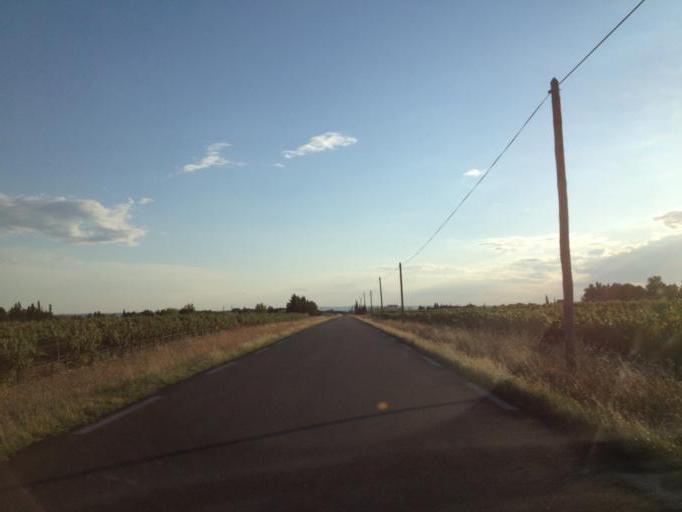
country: FR
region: Provence-Alpes-Cote d'Azur
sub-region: Departement du Vaucluse
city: Violes
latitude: 44.1759
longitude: 4.9370
